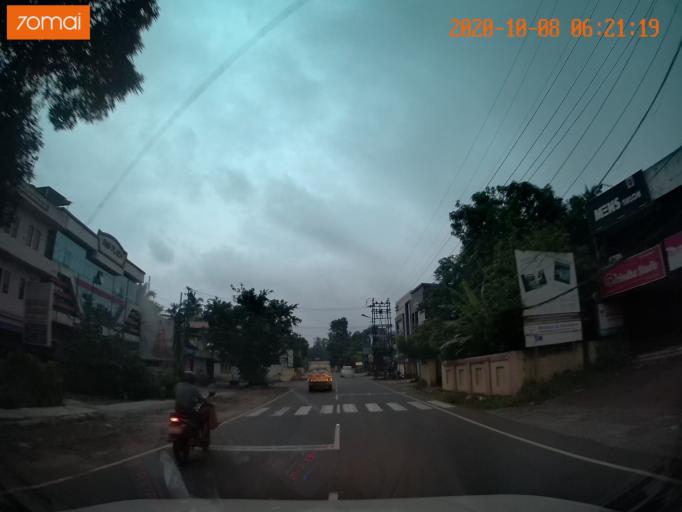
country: IN
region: Kerala
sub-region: Thrissur District
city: Trichur
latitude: 10.5200
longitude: 76.2327
